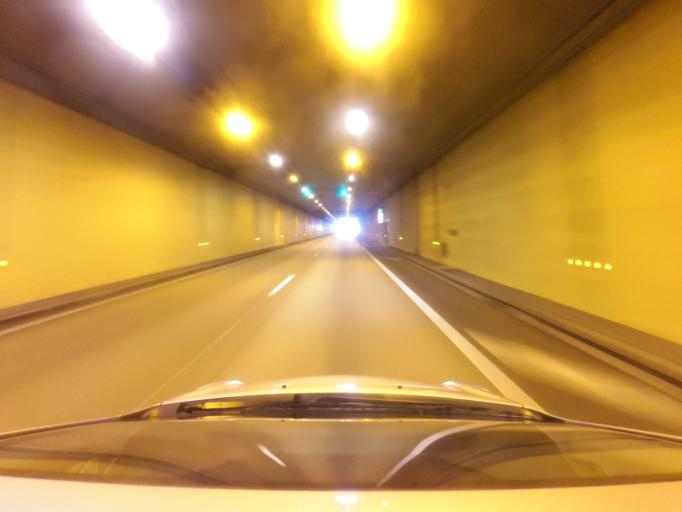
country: FR
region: Nord-Pas-de-Calais
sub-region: Departement du Pas-de-Calais
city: Nesles
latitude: 50.6404
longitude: 1.6656
